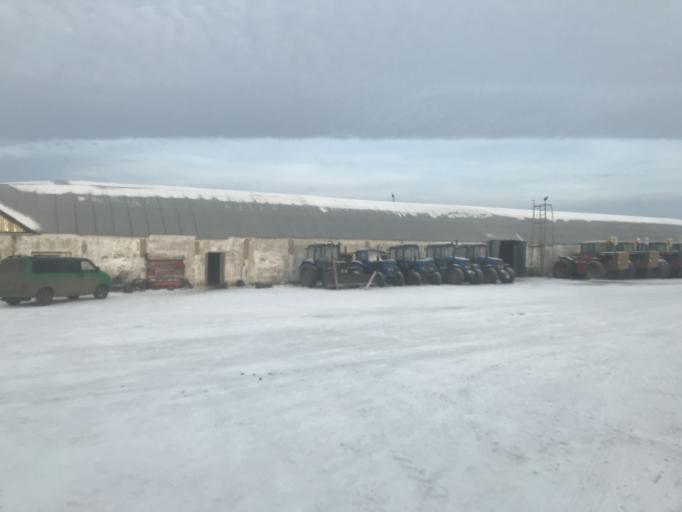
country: KZ
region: Soltustik Qazaqstan
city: Smirnovo
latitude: 54.8471
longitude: 69.7195
